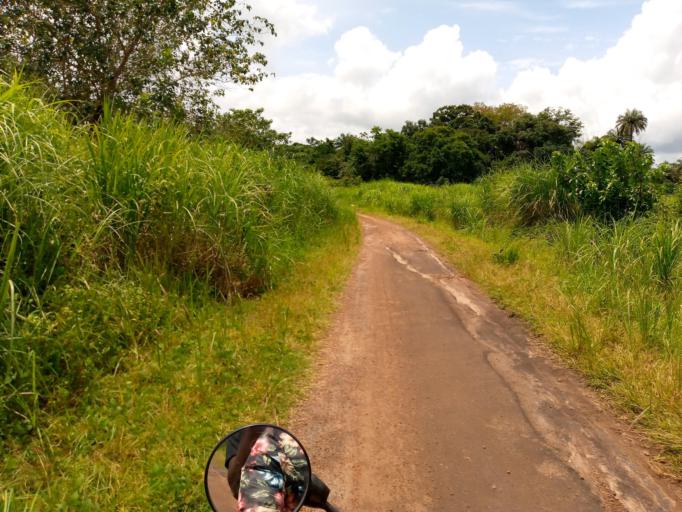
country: SL
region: Northern Province
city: Binkolo
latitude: 9.1120
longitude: -12.1371
